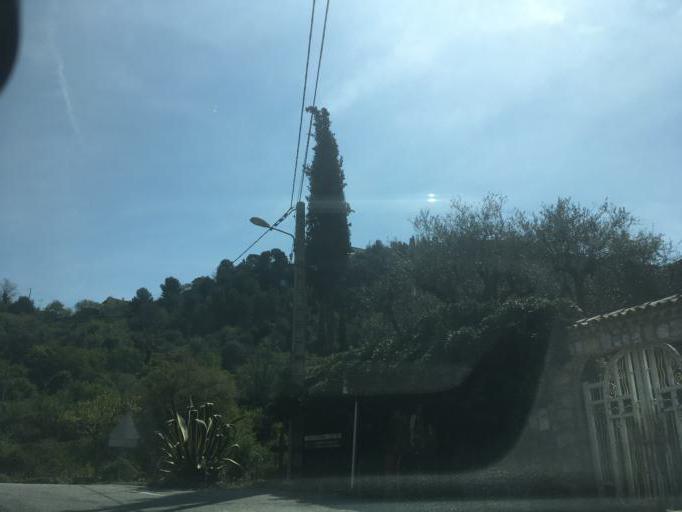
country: FR
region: Provence-Alpes-Cote d'Azur
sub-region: Departement des Alpes-Maritimes
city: Saint-Martin-du-Var
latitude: 43.8309
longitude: 7.1987
